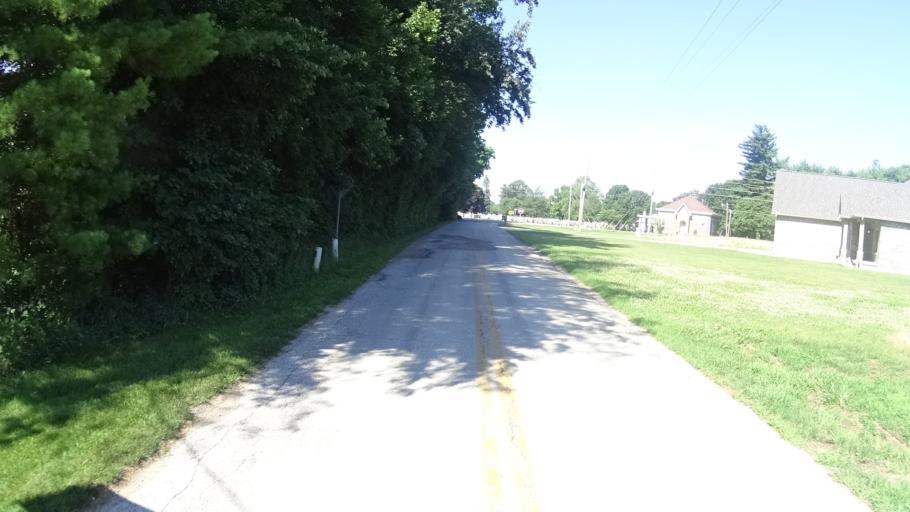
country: US
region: Indiana
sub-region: Hancock County
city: Fortville
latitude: 39.9589
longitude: -85.8422
